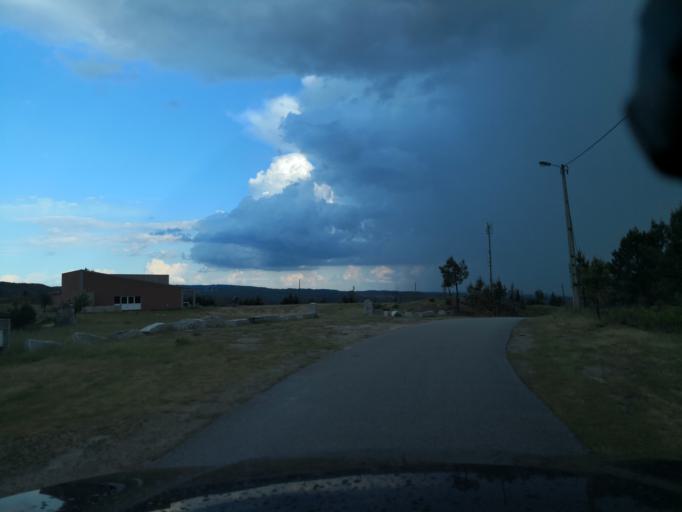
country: PT
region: Vila Real
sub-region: Vila Real
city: Vila Real
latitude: 41.3729
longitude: -7.7141
